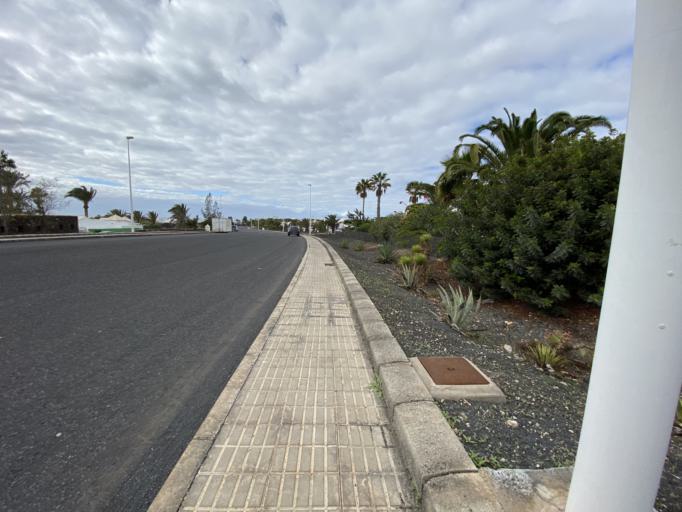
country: ES
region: Canary Islands
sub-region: Provincia de Las Palmas
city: Playa Blanca
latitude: 28.8638
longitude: -13.8470
